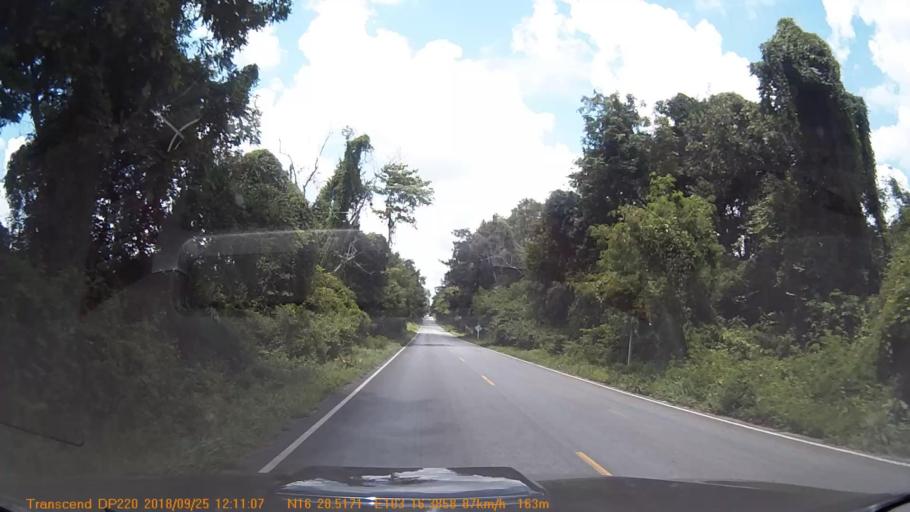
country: TH
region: Kalasin
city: Huai Mek
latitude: 16.4753
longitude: 103.2731
